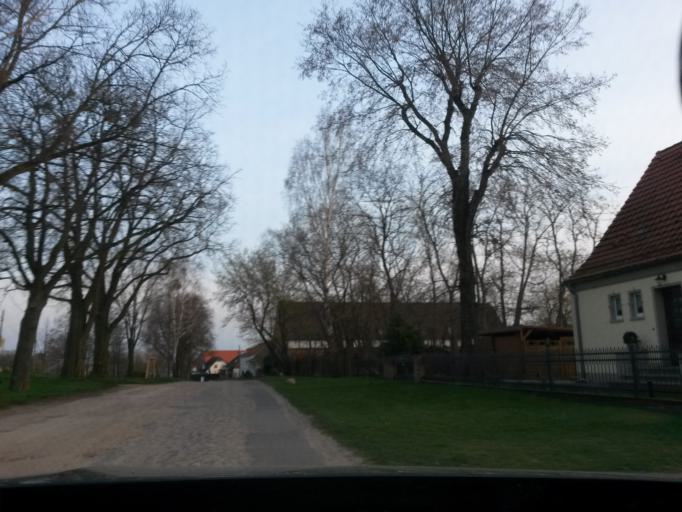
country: DE
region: Brandenburg
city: Protzel
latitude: 52.5693
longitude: 13.9673
